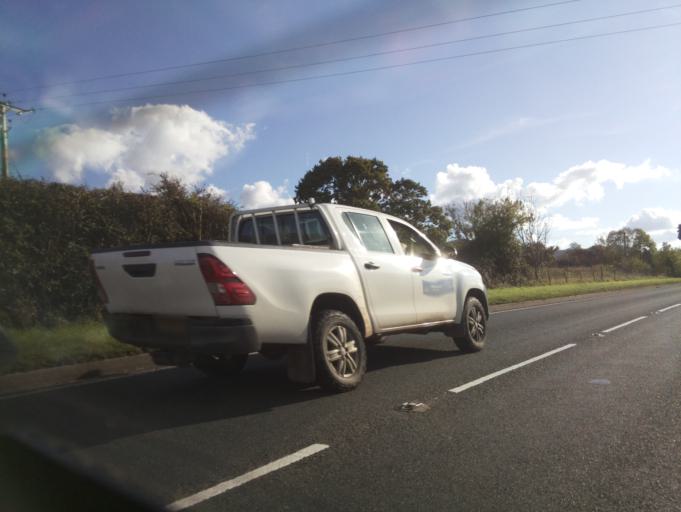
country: GB
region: Wales
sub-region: Sir Powys
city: Hay
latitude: 52.0353
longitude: -3.2031
